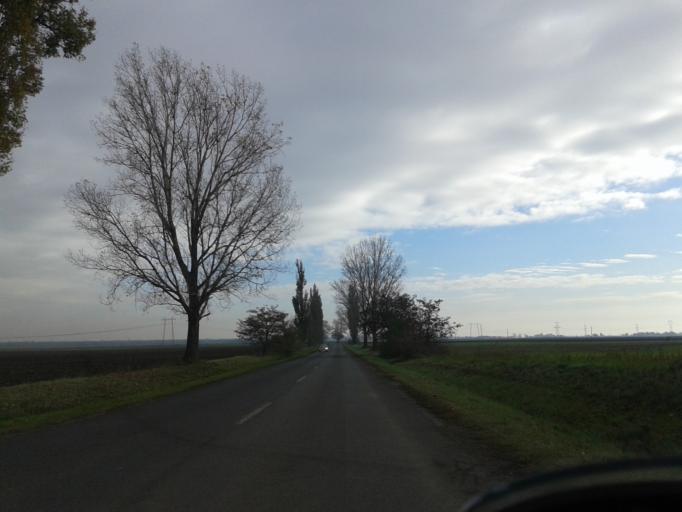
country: HU
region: Fejer
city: Pusztaszabolcs
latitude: 47.1357
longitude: 18.7830
